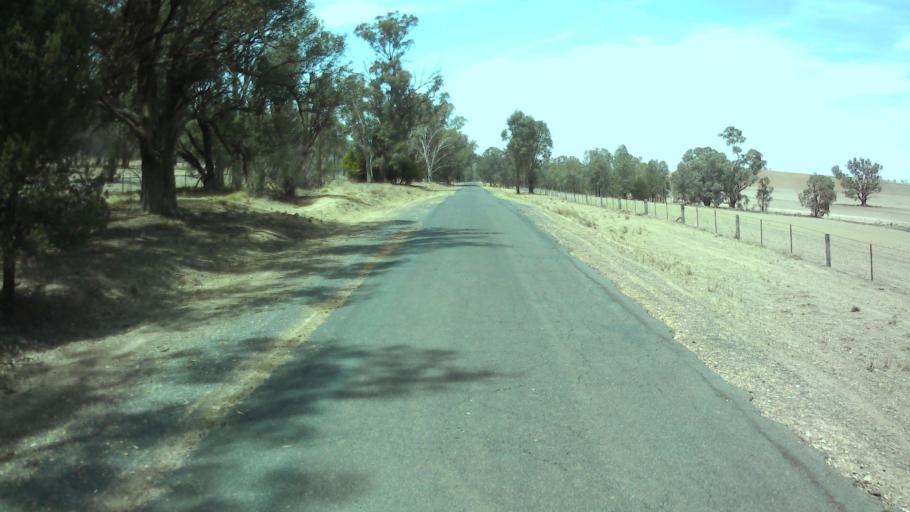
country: AU
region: New South Wales
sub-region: Weddin
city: Grenfell
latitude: -34.0240
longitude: 148.4320
